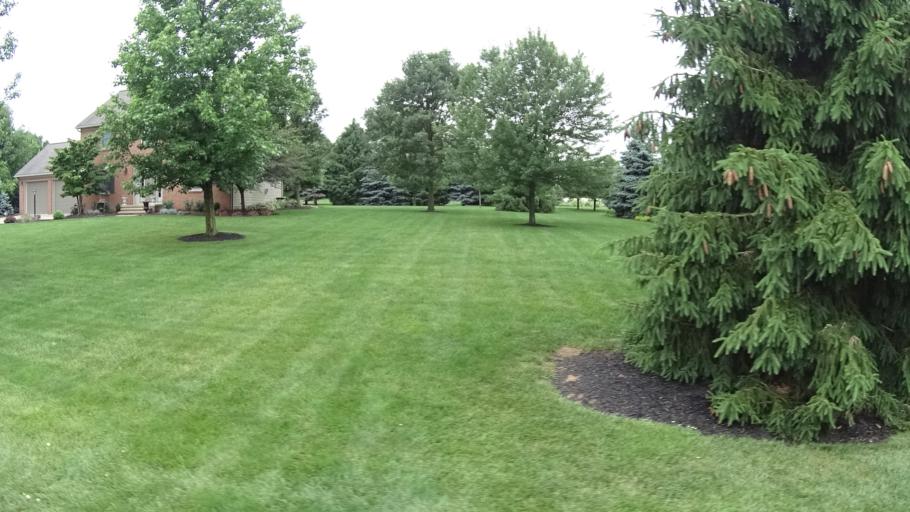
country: US
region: Ohio
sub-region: Erie County
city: Milan
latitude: 41.3006
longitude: -82.5798
